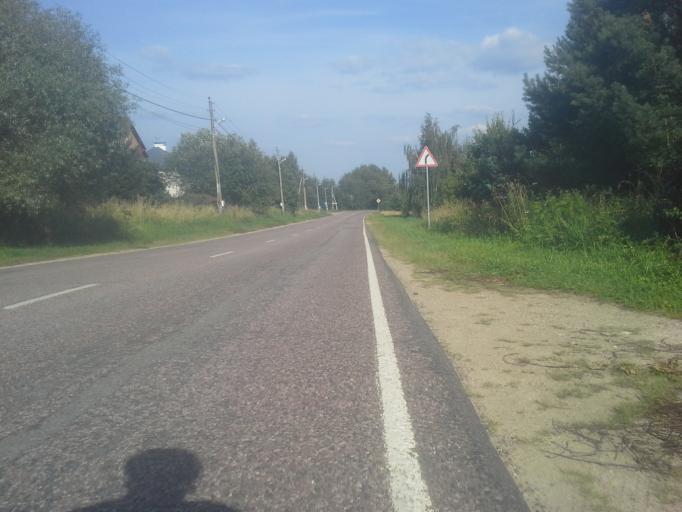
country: RU
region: Moskovskaya
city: Karinskoye
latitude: 55.7852
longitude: 36.6718
